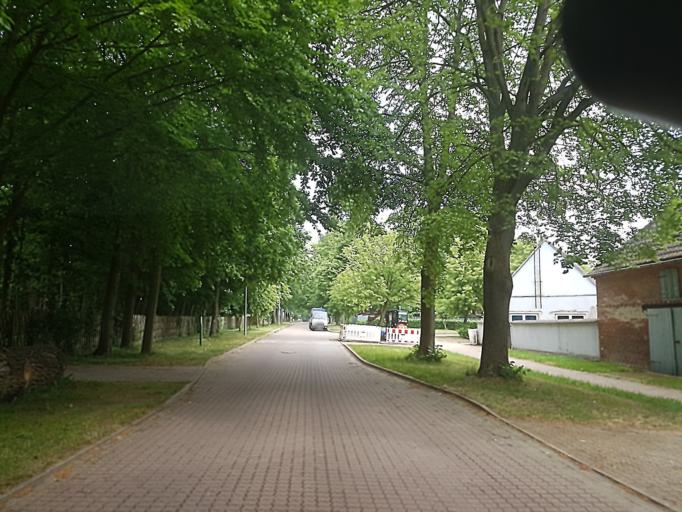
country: DE
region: Saxony-Anhalt
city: Lindau
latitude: 52.0780
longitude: 12.2416
